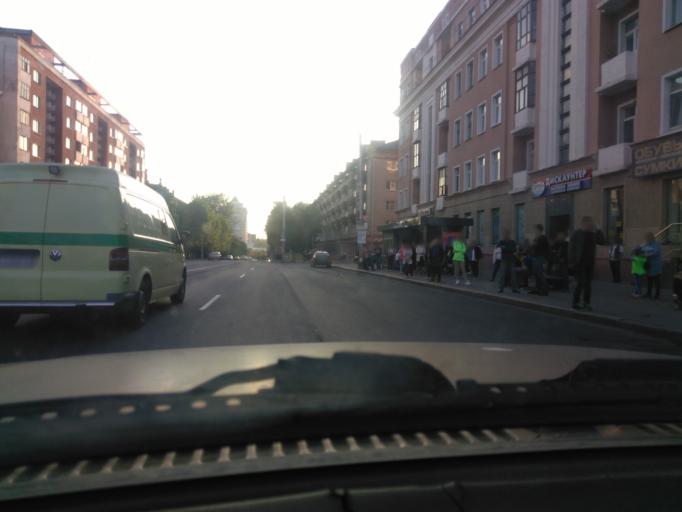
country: BY
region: Mogilev
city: Mahilyow
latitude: 53.9090
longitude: 30.3396
